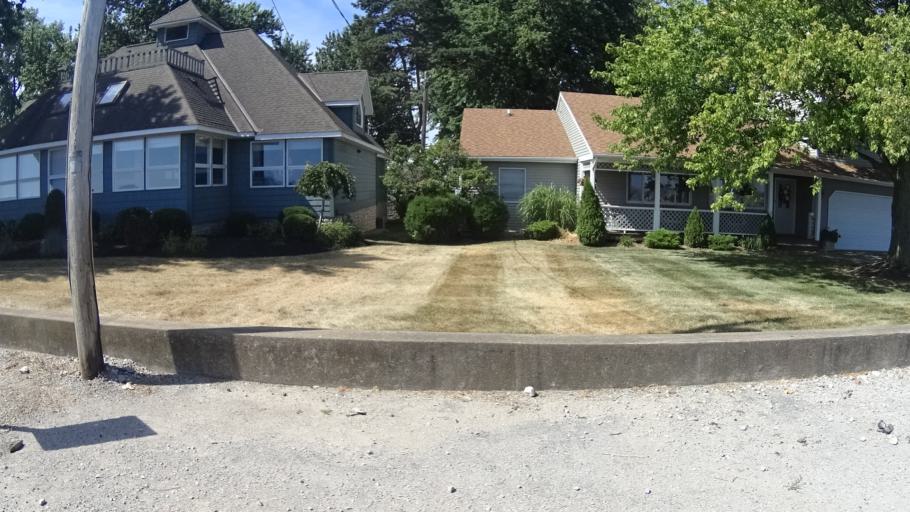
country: US
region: Ohio
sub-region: Erie County
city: Huron
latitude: 41.4341
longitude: -82.6223
